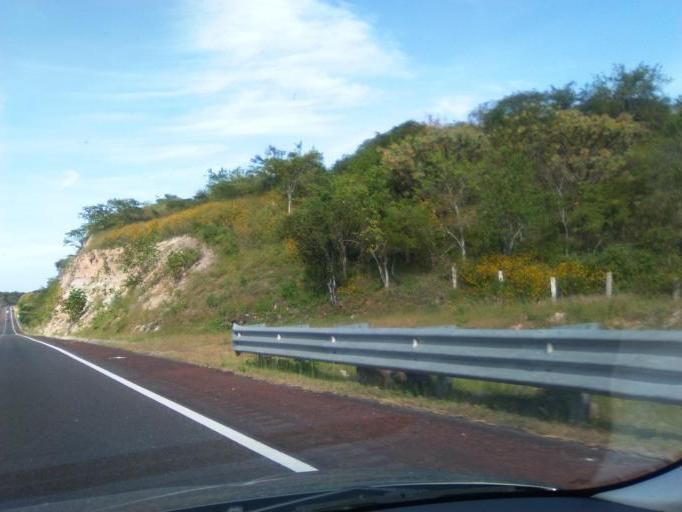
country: MX
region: Guerrero
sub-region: Huitzuco de los Figueroa
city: San Francisco Ozomatlan
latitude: 18.0573
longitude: -99.2487
